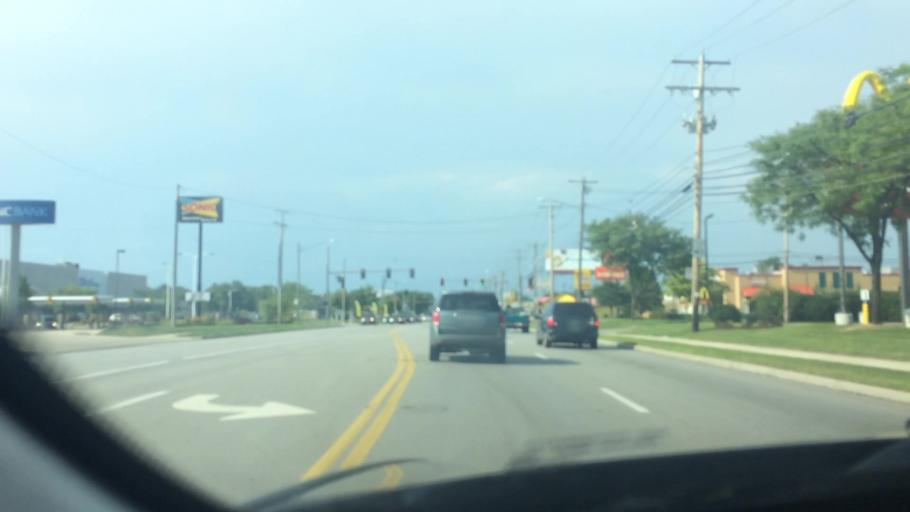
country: US
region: Ohio
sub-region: Lucas County
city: Ottawa Hills
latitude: 41.6784
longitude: -83.6227
